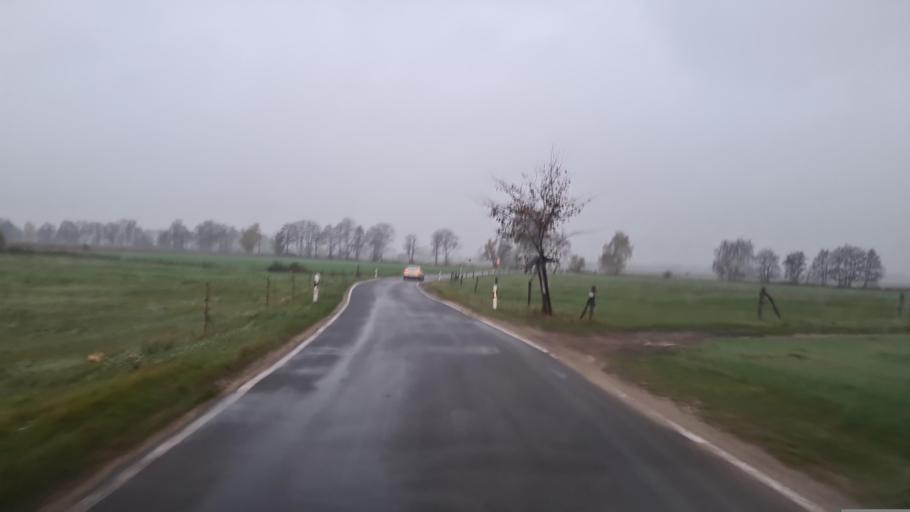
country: DE
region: Brandenburg
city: Beelitz
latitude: 52.2415
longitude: 13.0123
